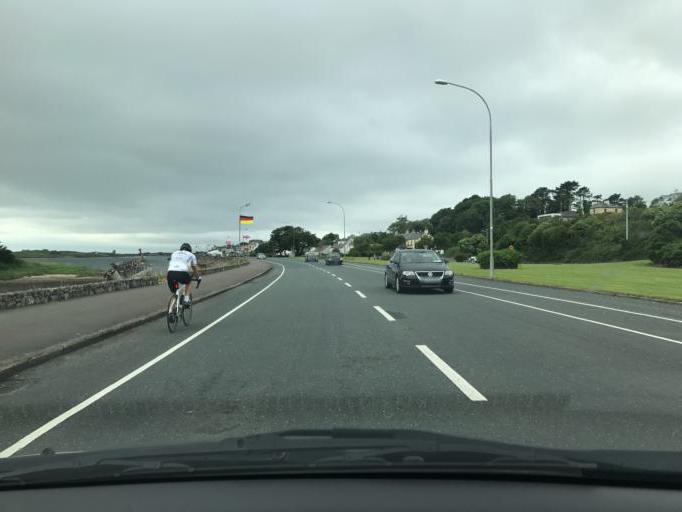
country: IE
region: Connaught
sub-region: Sligo
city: Strandhill
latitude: 54.3061
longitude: -8.5503
